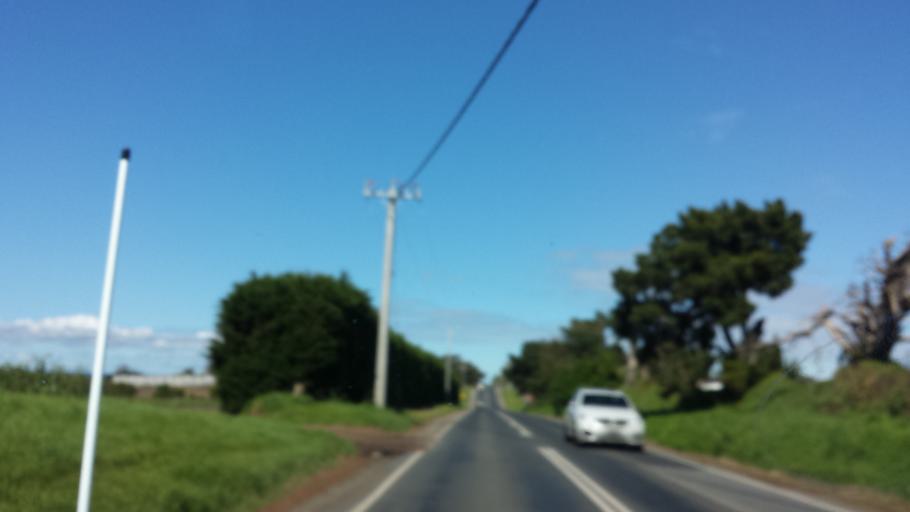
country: AU
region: Victoria
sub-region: Casey
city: Junction Village
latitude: -38.1497
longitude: 145.3209
